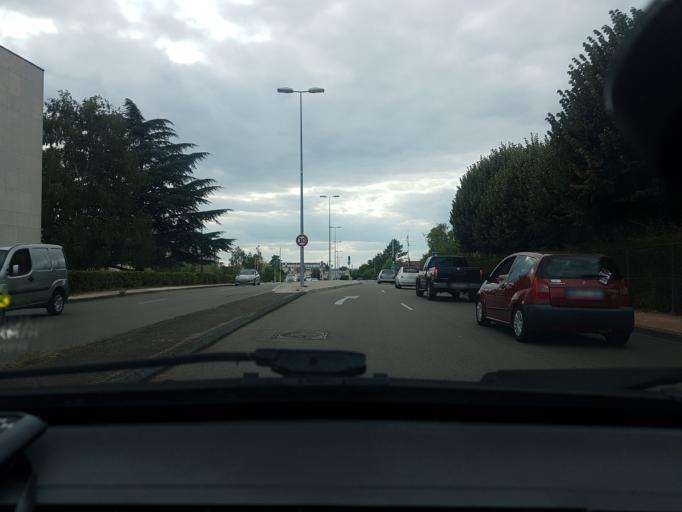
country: FR
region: Bourgogne
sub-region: Departement de la Cote-d'Or
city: Saint-Apollinaire
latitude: 47.3167
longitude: 5.0691
